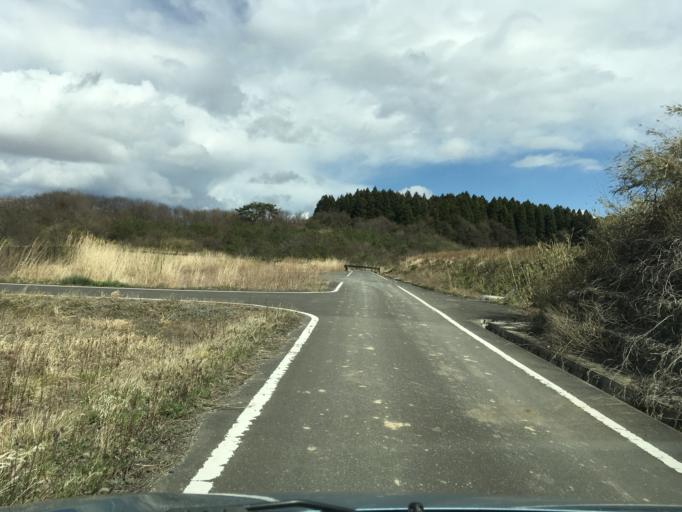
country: JP
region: Miyagi
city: Kogota
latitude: 38.6863
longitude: 141.1008
